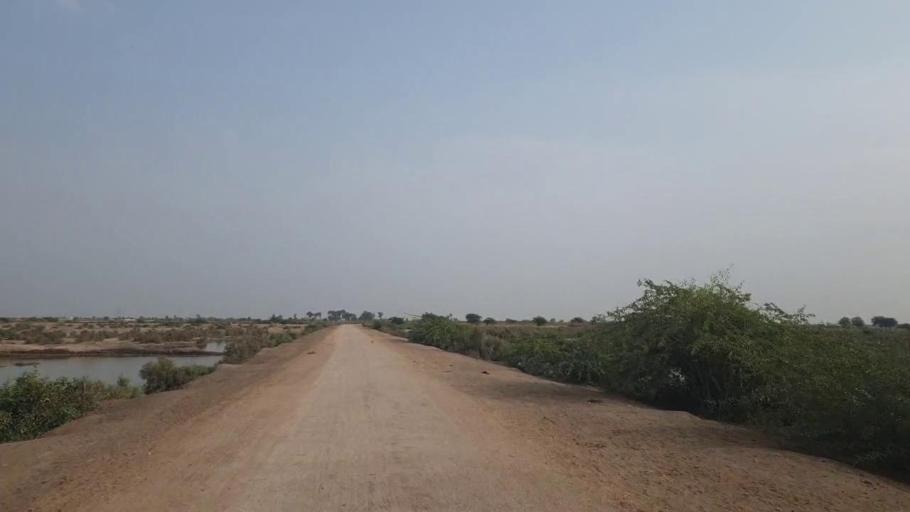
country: PK
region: Sindh
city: Badin
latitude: 24.6062
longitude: 68.6907
